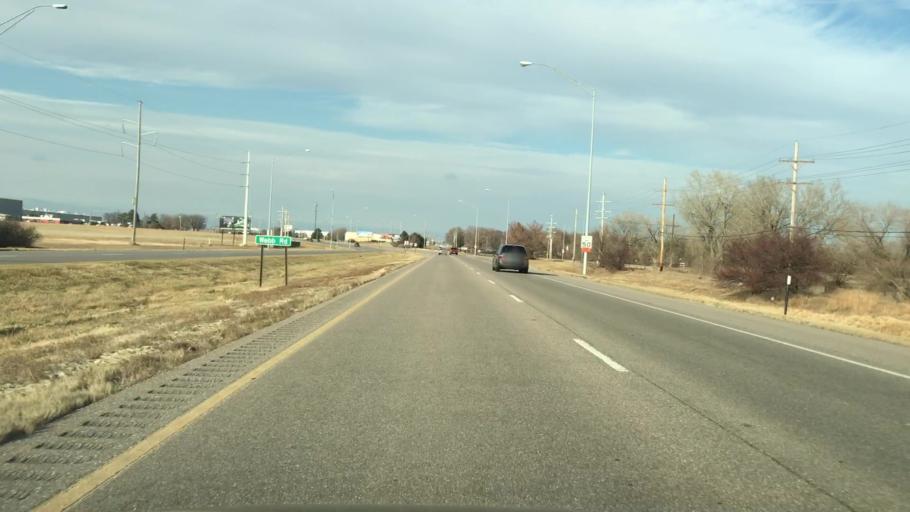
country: US
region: Nebraska
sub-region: Hall County
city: Grand Island
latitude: 40.8934
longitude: -98.3783
